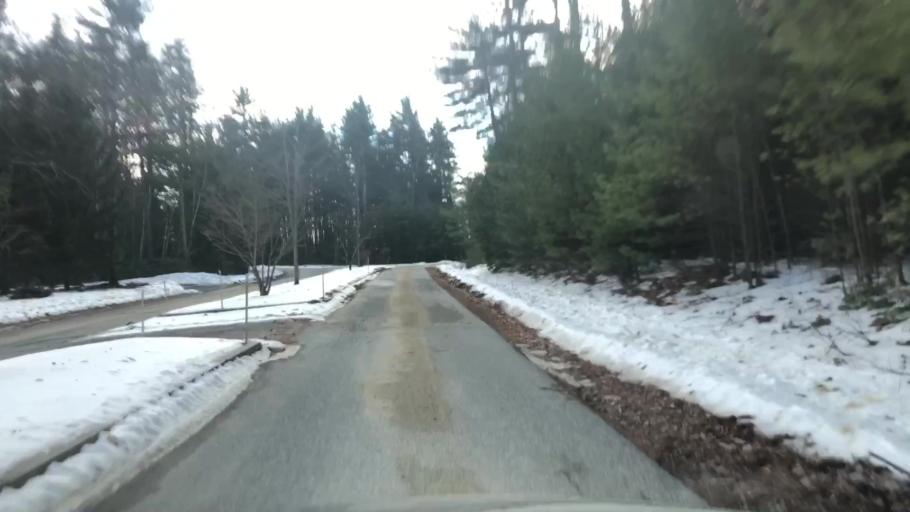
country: US
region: New Hampshire
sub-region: Hillsborough County
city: Milford
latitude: 42.8483
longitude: -71.6208
